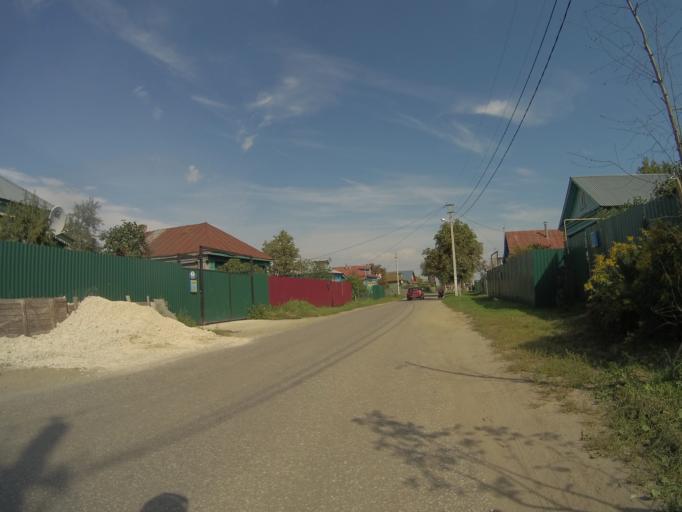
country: RU
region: Vladimir
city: Bogolyubovo
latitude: 56.1105
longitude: 40.5347
